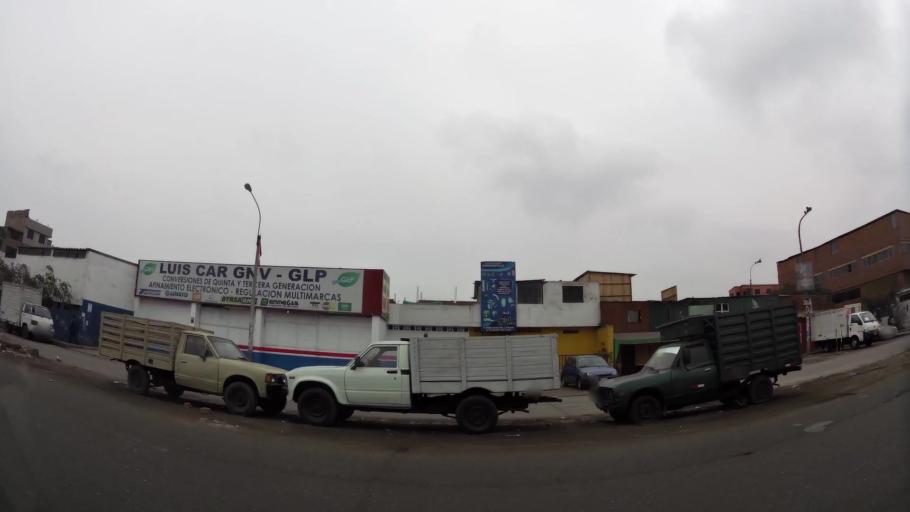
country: PE
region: Lima
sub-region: Lima
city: San Luis
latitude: -12.0737
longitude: -77.0060
